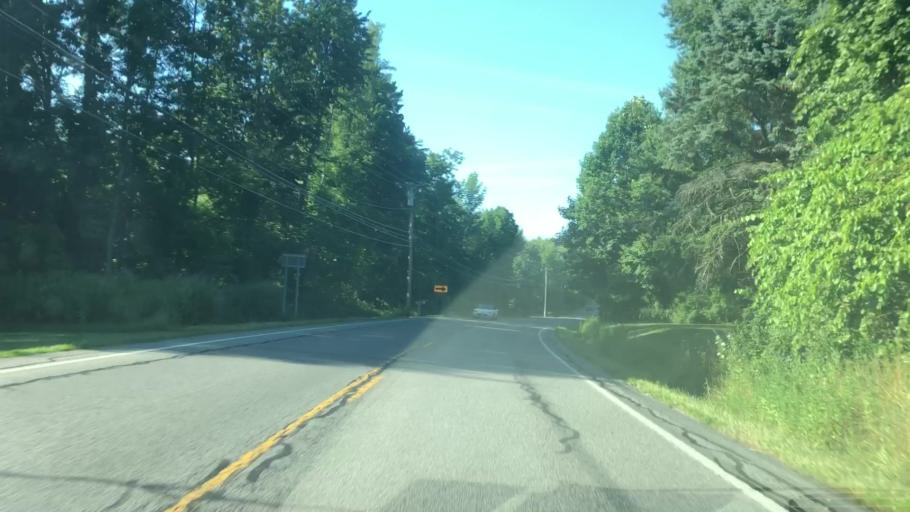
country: US
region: New York
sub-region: Wayne County
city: Ontario
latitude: 43.1529
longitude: -77.2926
